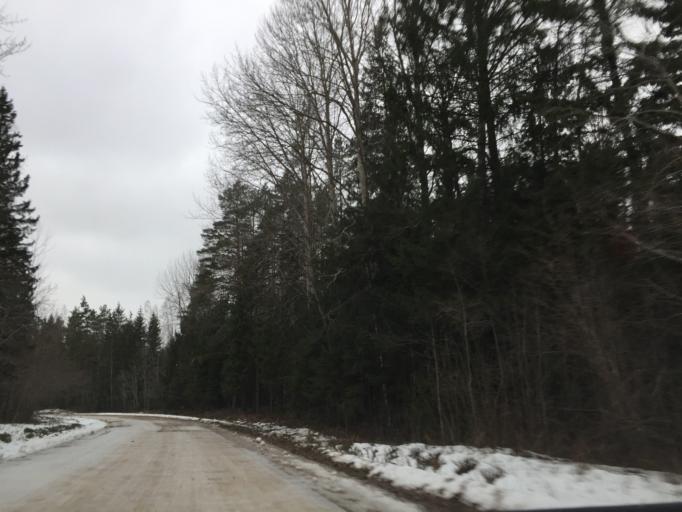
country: LV
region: Salacgrivas
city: Salacgriva
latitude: 57.6497
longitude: 24.4322
